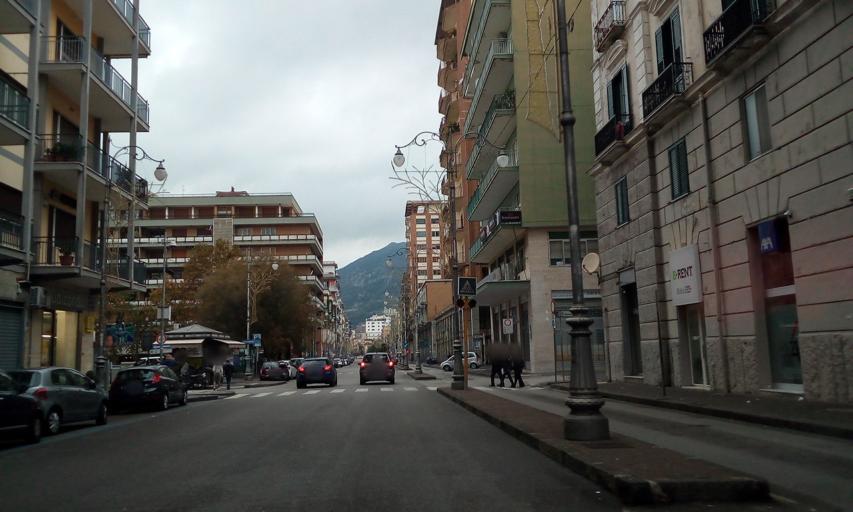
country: IT
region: Campania
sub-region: Provincia di Salerno
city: Salerno
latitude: 40.6748
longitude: 14.7712
